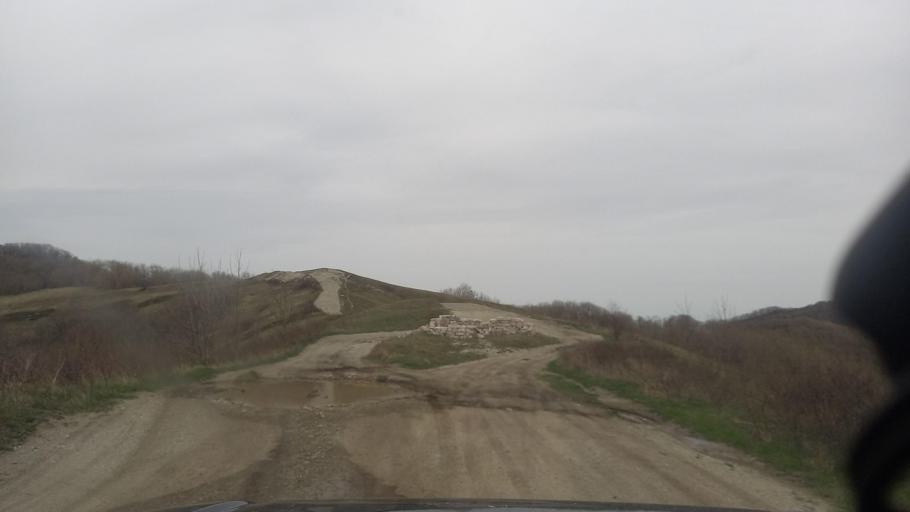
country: RU
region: Krasnodarskiy
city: Divnomorskoye
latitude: 44.6106
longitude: 38.2221
